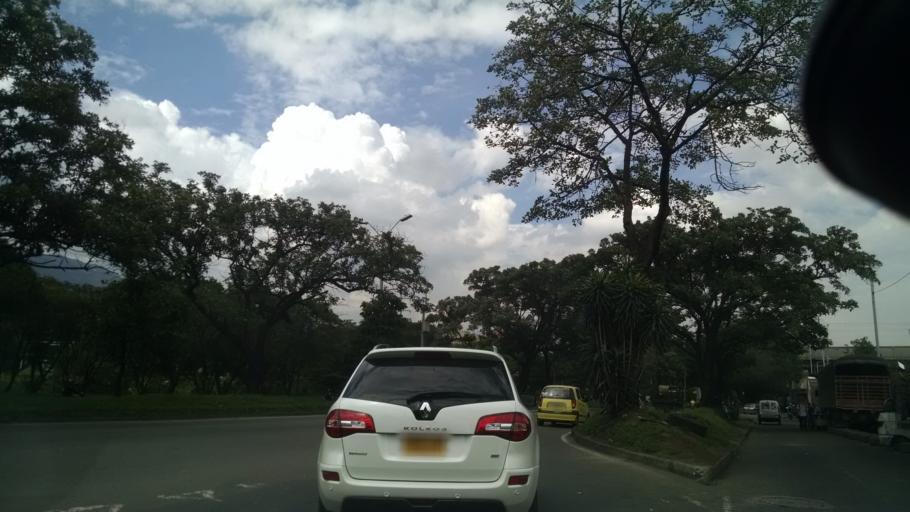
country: CO
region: Antioquia
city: Medellin
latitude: 6.2493
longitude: -75.5792
